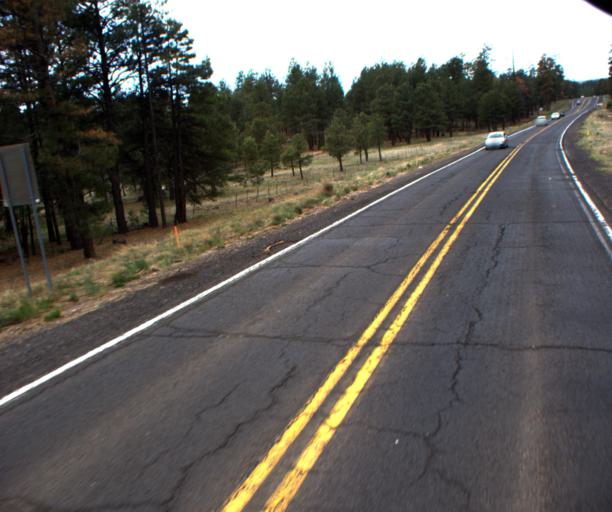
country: US
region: Arizona
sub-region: Coconino County
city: Kachina Village
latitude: 35.1229
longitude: -111.6976
